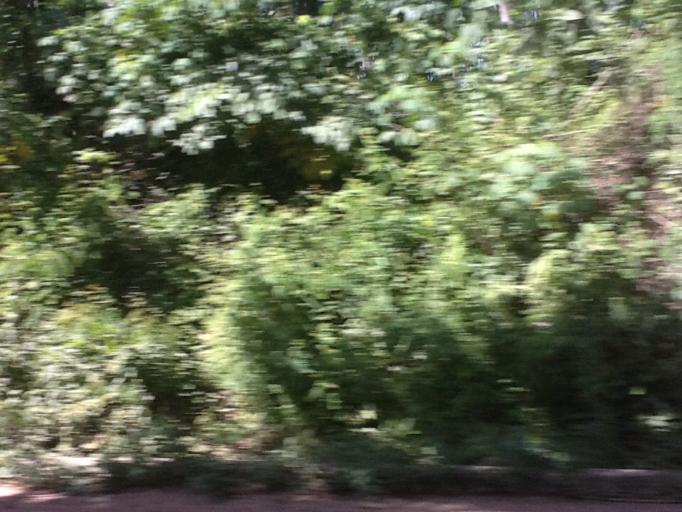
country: TH
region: Phuket
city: Thalang
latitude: 8.1213
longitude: 98.3280
